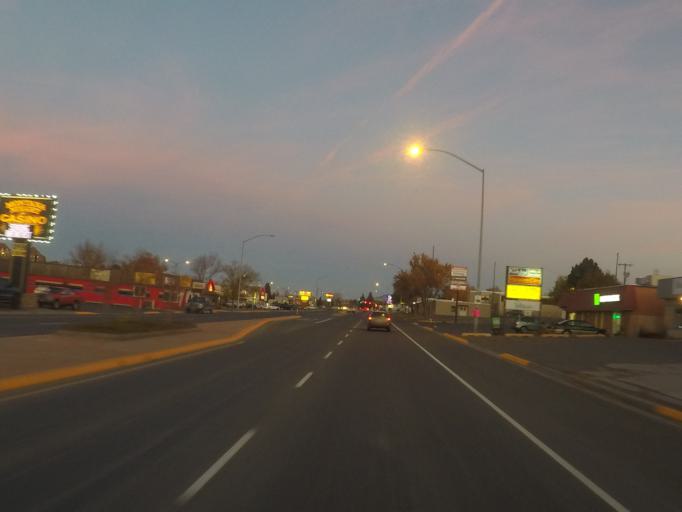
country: US
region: Montana
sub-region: Lewis and Clark County
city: Helena
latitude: 46.6003
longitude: -112.0483
